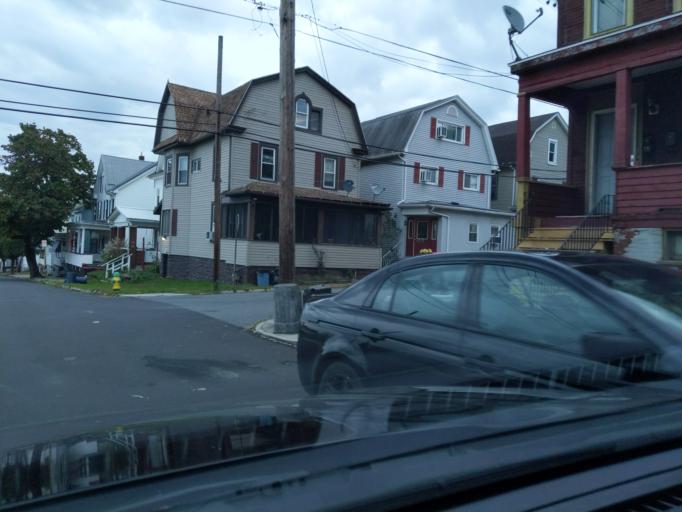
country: US
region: Pennsylvania
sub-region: Blair County
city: Altoona
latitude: 40.5132
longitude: -78.3902
